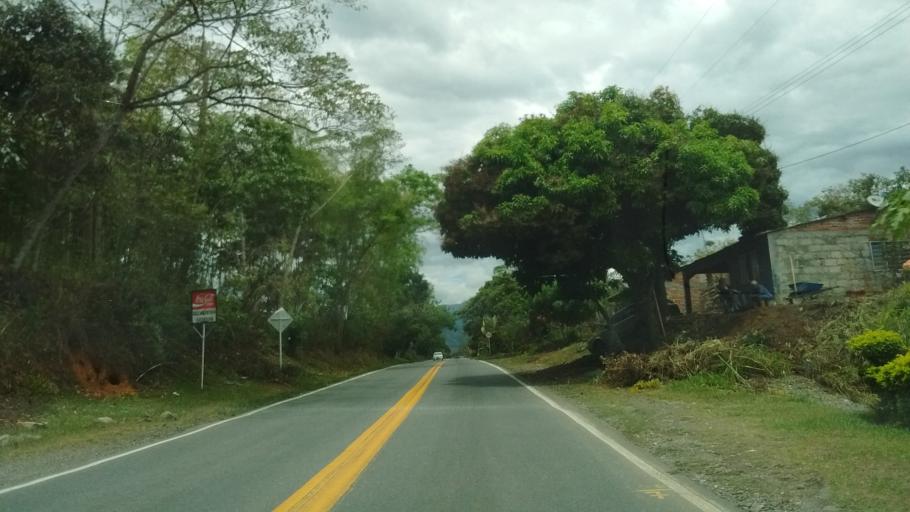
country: CO
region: Cauca
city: La Sierra
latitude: 2.2303
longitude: -76.7911
